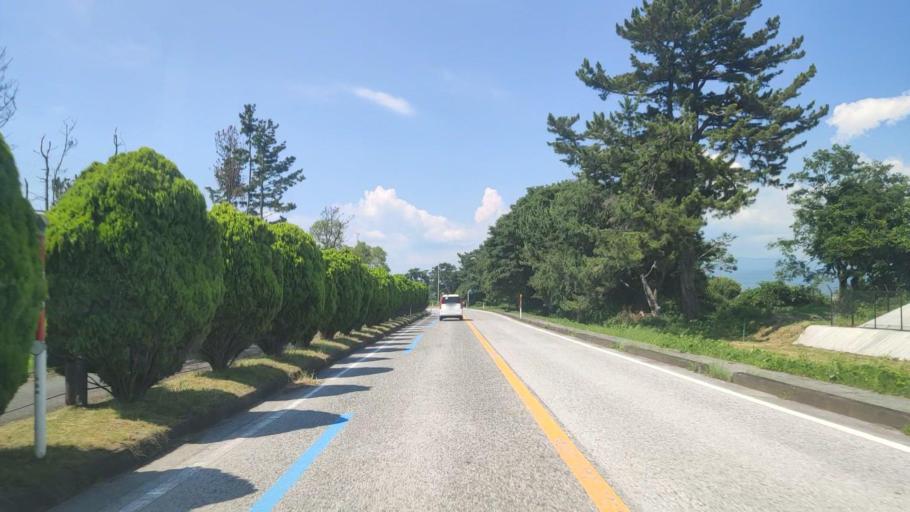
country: JP
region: Shiga Prefecture
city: Nagahama
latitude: 35.3952
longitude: 136.2179
